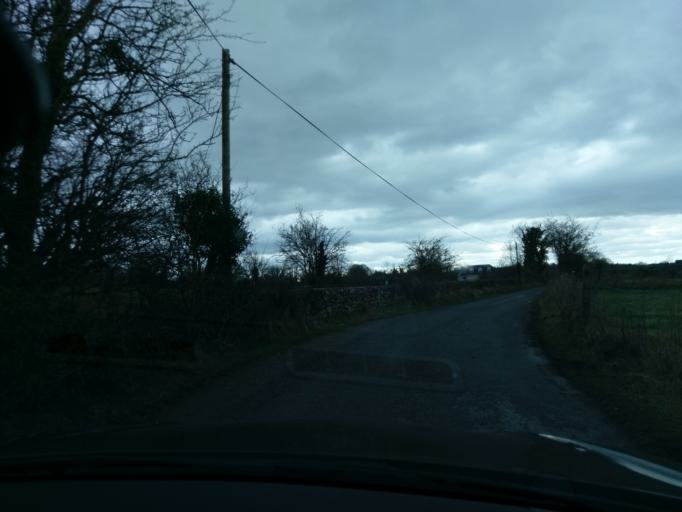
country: IE
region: Connaught
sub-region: County Galway
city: Athenry
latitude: 53.3871
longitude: -8.6574
